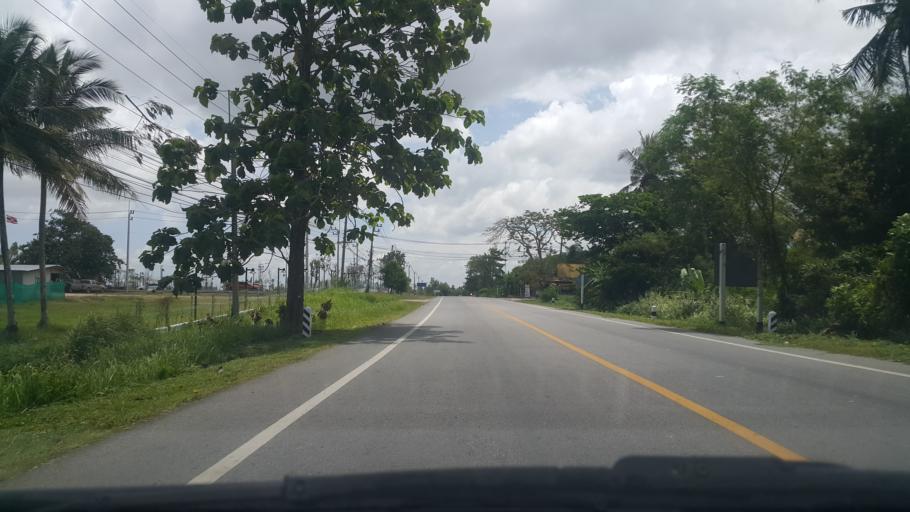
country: TH
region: Rayong
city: Ban Chang
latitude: 12.7773
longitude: 101.0259
